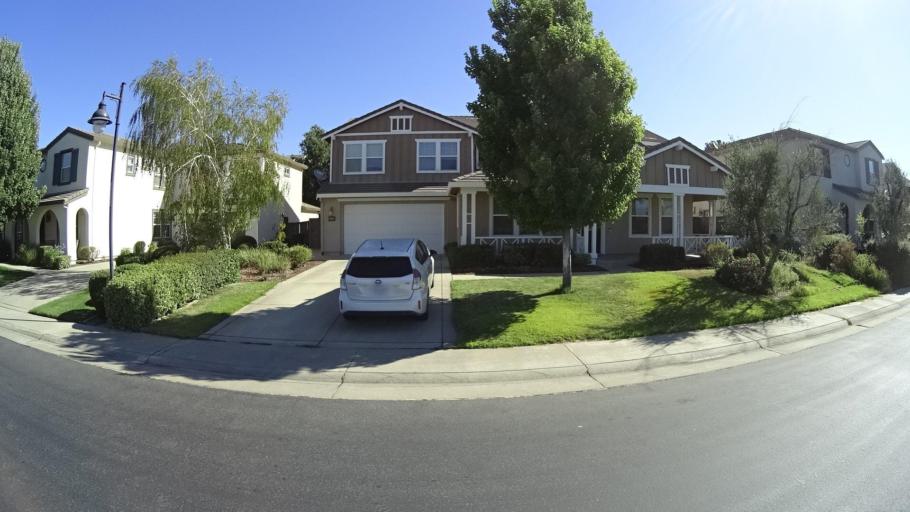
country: US
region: California
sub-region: Placer County
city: Lincoln
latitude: 38.8342
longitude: -121.2777
